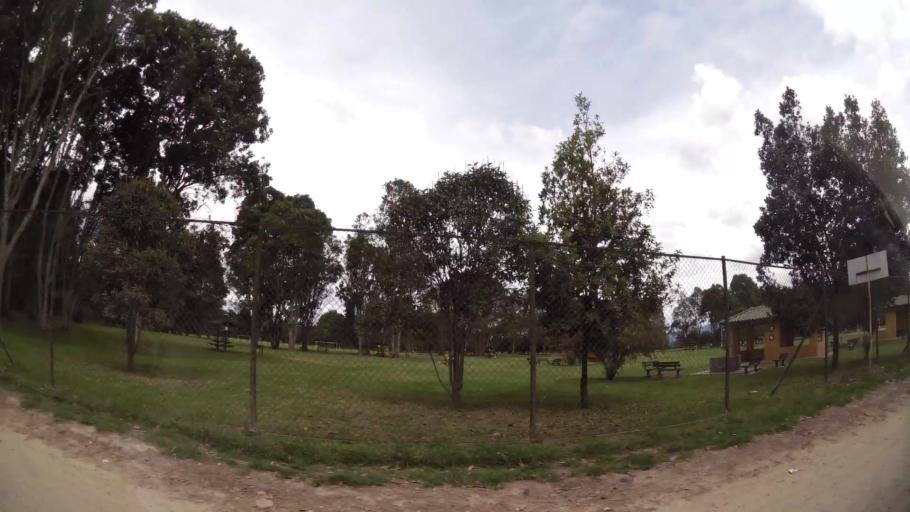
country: CO
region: Cundinamarca
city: Funza
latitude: 4.7333
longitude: -74.1474
